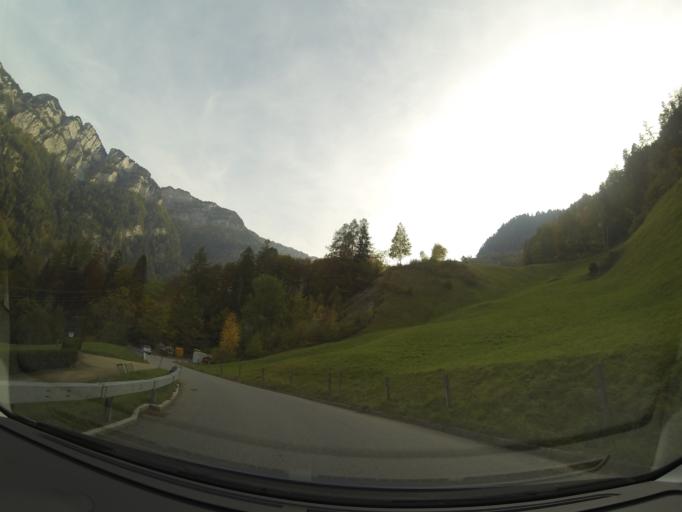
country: CH
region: Saint Gallen
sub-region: Wahlkreis Sarganserland
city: Bad Ragaz
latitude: 46.9502
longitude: 9.4764
